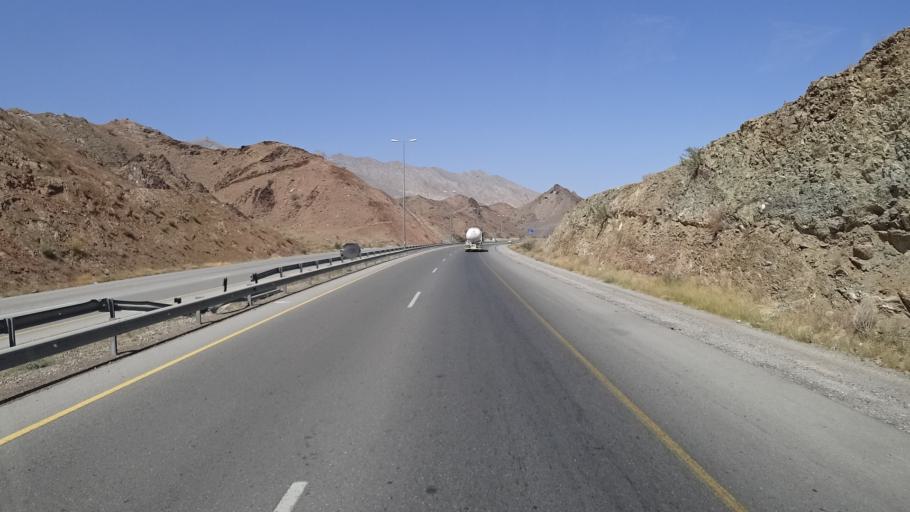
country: OM
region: Muhafazat ad Dakhiliyah
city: Sufalat Sama'il
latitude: 23.3056
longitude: 57.9425
